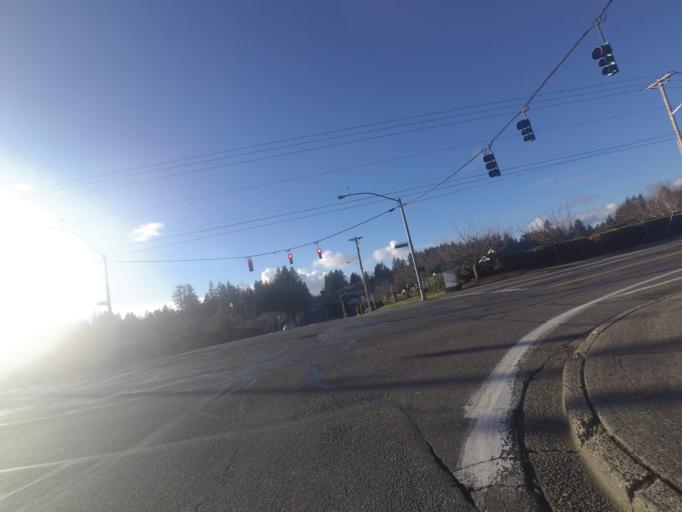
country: US
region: Washington
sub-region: Pierce County
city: Fircrest
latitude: 47.2210
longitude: -122.5262
